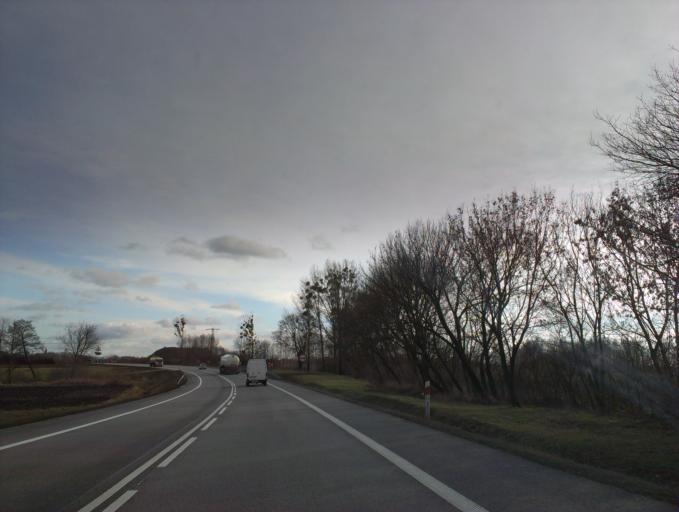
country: PL
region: Kujawsko-Pomorskie
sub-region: Powiat lipnowski
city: Kikol
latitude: 52.9201
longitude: 19.0969
